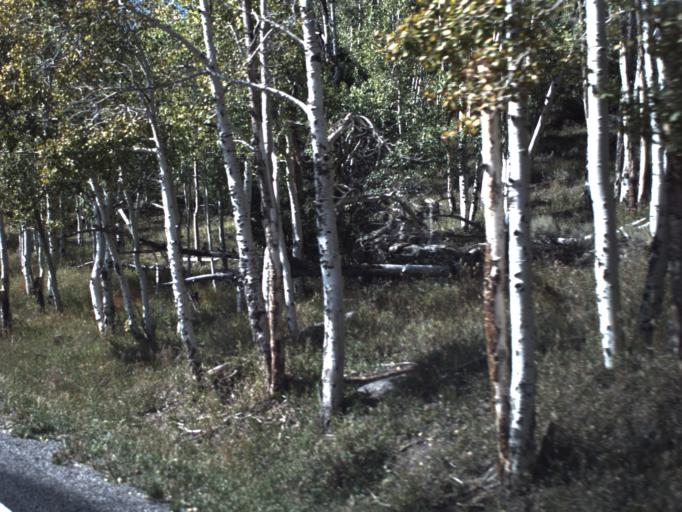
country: US
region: Utah
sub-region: Wayne County
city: Loa
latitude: 38.5184
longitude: -111.7576
